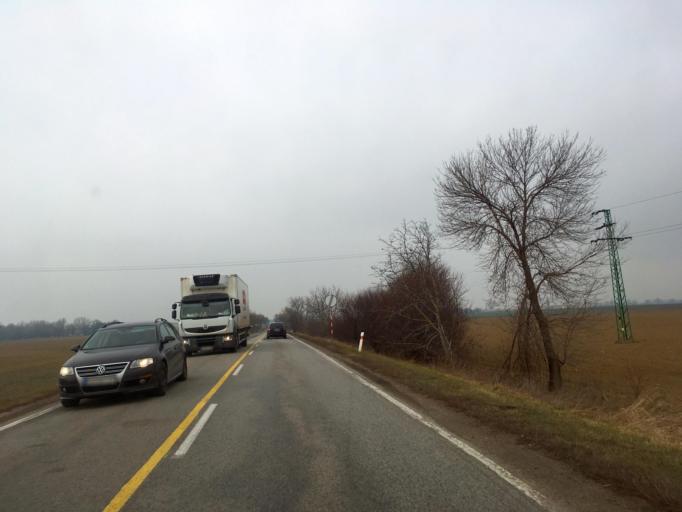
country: SK
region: Nitriansky
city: Sellye
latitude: 48.2322
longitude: 17.8355
